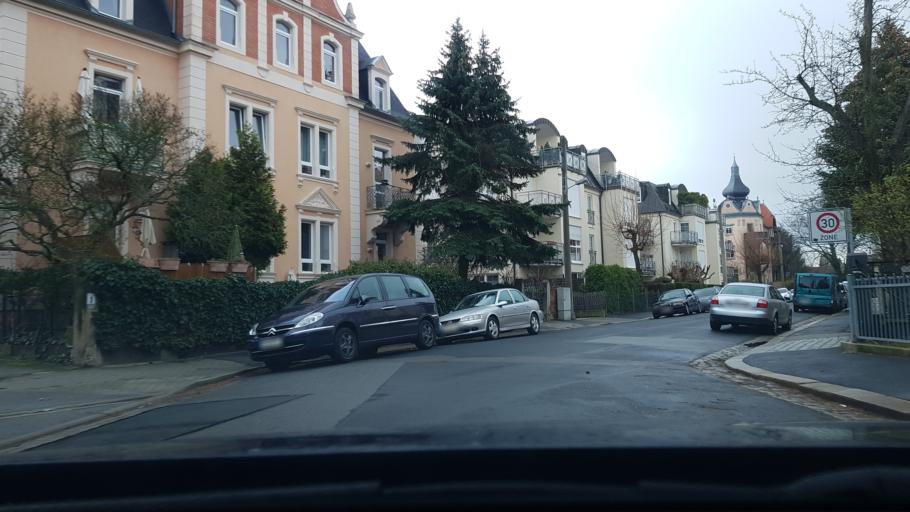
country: DE
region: Saxony
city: Heidenau
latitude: 51.0228
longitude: 13.8346
